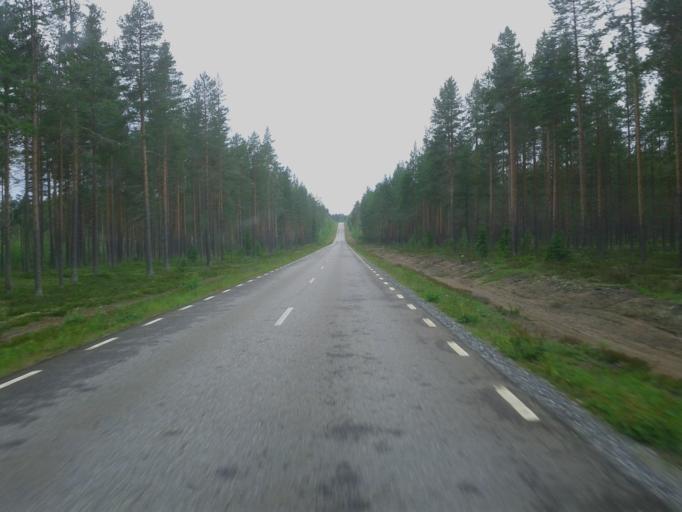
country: SE
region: Vaesterbotten
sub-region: Skelleftea Kommun
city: Kage
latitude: 64.9186
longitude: 20.9287
